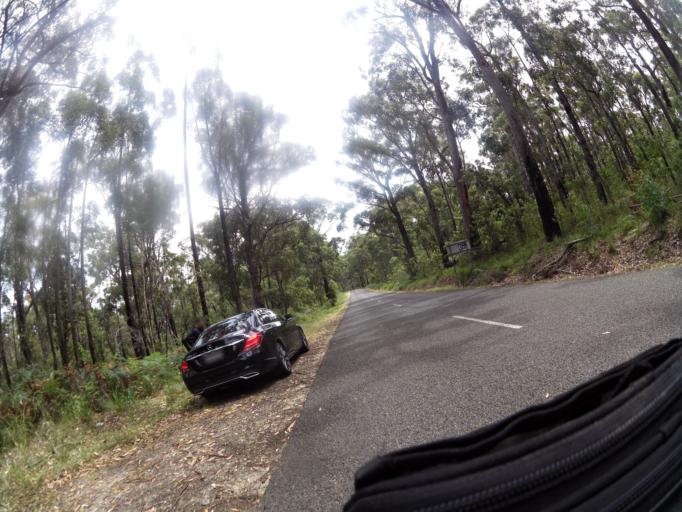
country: AU
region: Victoria
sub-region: East Gippsland
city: Lakes Entrance
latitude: -37.6970
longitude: 148.7413
